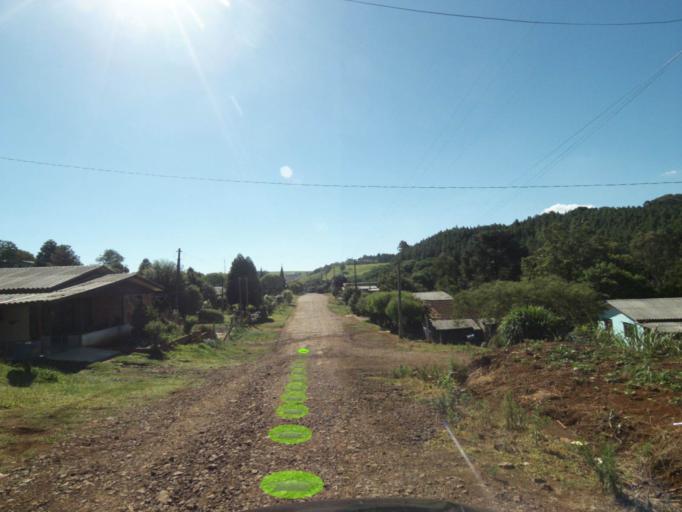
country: BR
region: Parana
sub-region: Coronel Vivida
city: Coronel Vivida
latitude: -26.1431
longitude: -52.3760
